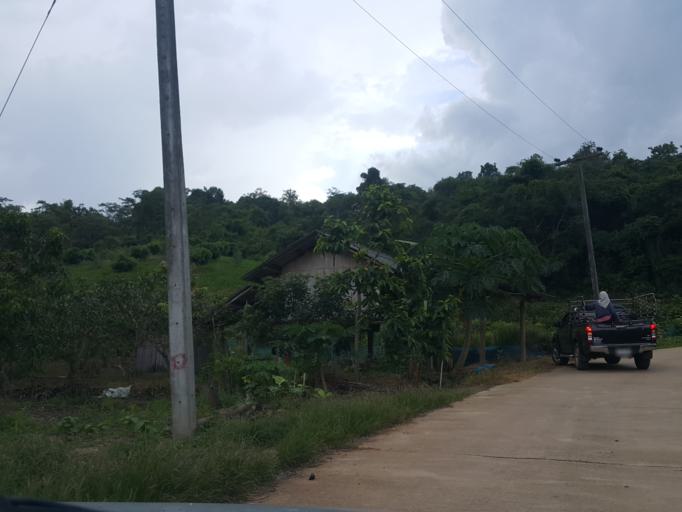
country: TH
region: Chiang Mai
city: Phrao
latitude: 19.3239
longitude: 99.1329
